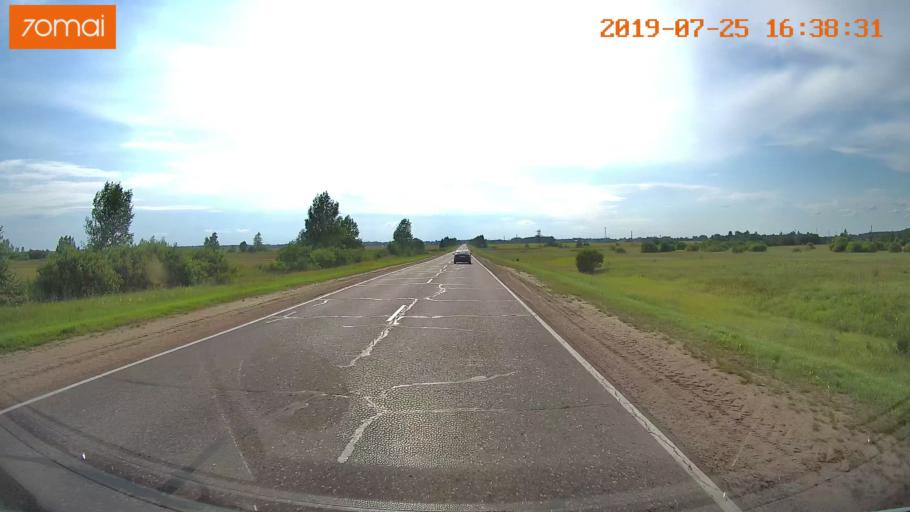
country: RU
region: Ivanovo
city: Privolzhsk
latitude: 57.3876
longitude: 41.3484
